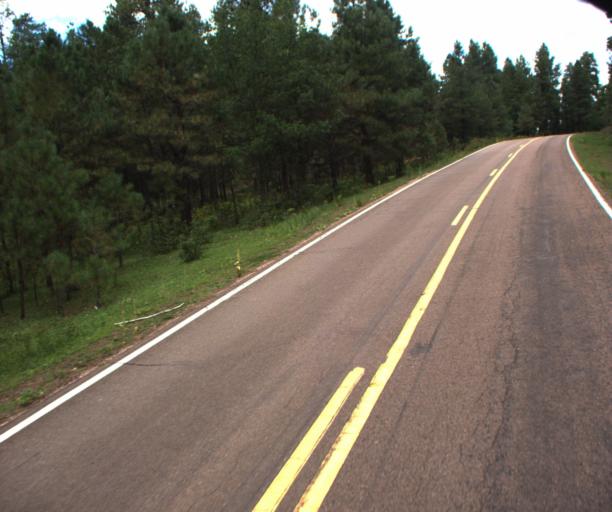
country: US
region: Arizona
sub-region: Navajo County
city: Pinetop-Lakeside
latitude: 34.0355
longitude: -109.7532
